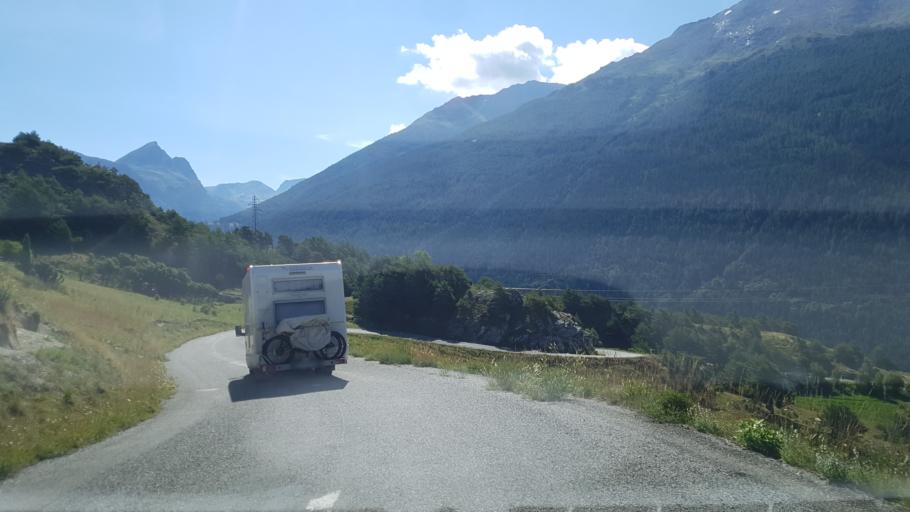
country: FR
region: Rhone-Alpes
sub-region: Departement de la Savoie
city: Modane
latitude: 45.2171
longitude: 6.7382
